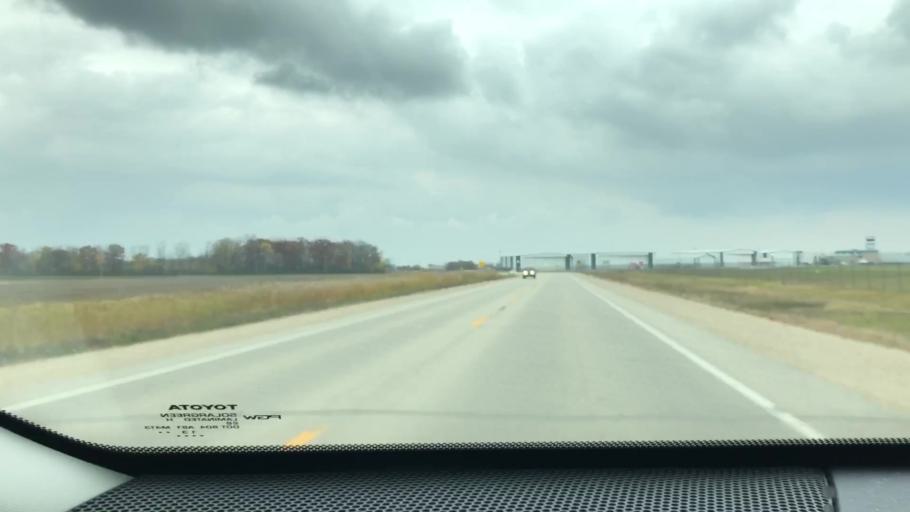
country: US
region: Wisconsin
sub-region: Brown County
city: Oneida
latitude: 44.4966
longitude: -88.1361
